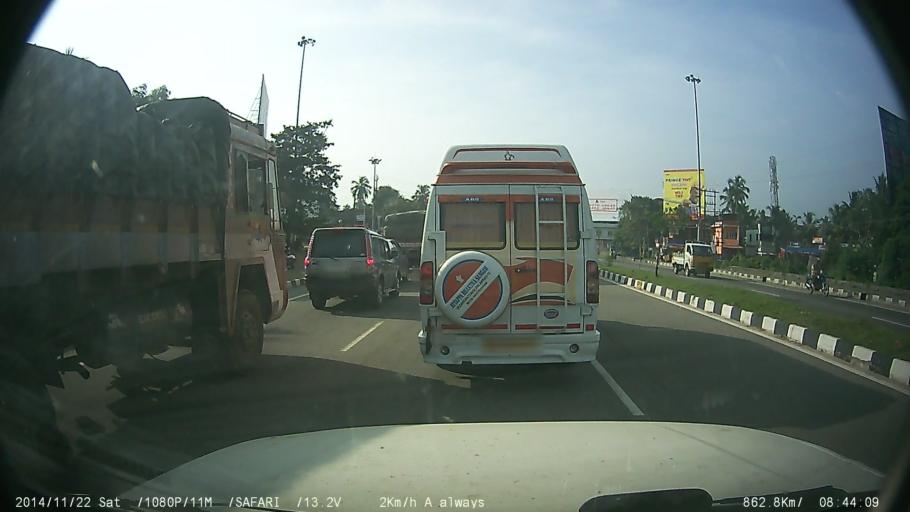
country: IN
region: Kerala
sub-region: Thrissur District
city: Trichur
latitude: 10.5120
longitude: 76.2585
